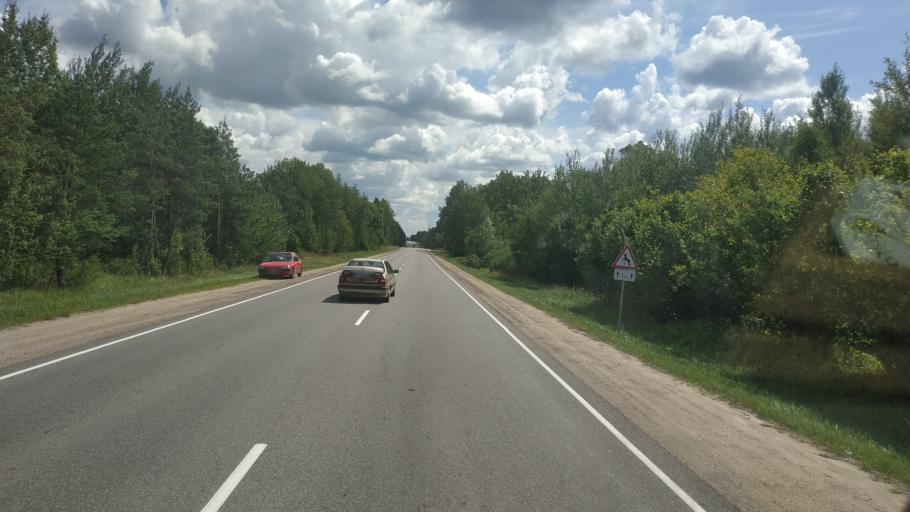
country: BY
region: Mogilev
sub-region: Mahilyowski Rayon
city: Veyno
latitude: 53.8256
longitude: 30.4213
